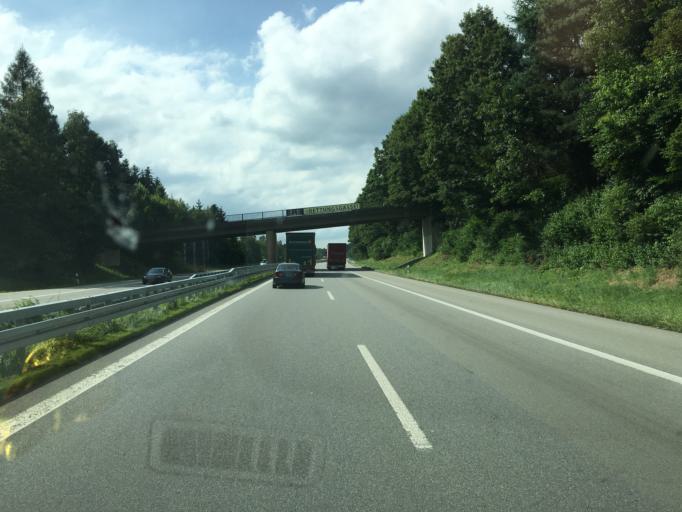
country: DE
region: Bavaria
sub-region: Lower Bavaria
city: Tiefenbach
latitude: 48.6129
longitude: 13.3605
